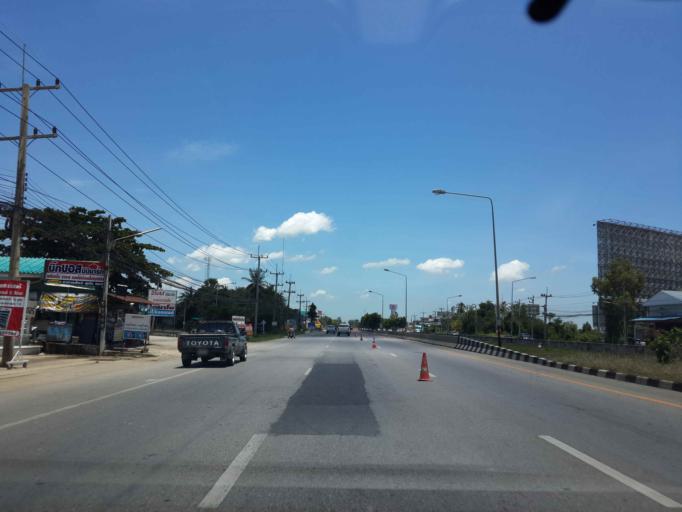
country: TH
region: Phetchaburi
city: Tha Yang
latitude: 12.9891
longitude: 99.9025
